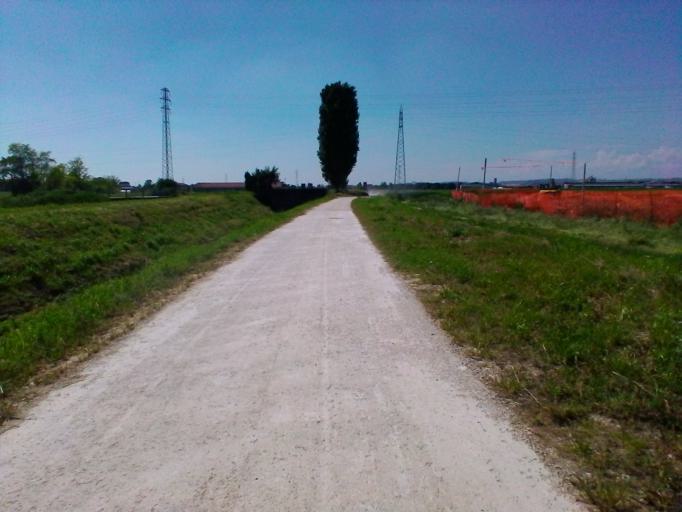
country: IT
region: Veneto
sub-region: Provincia di Verona
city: Povegliano Veronese
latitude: 45.3404
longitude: 10.8656
